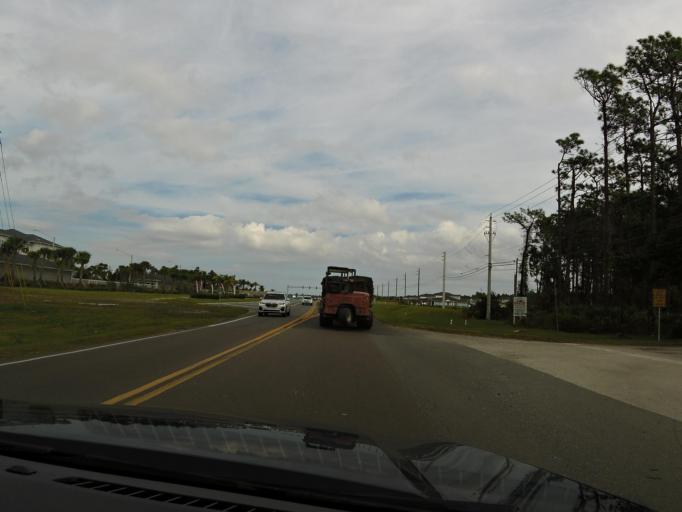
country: US
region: Florida
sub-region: Saint Johns County
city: Palm Valley
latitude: 30.0753
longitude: -81.4864
